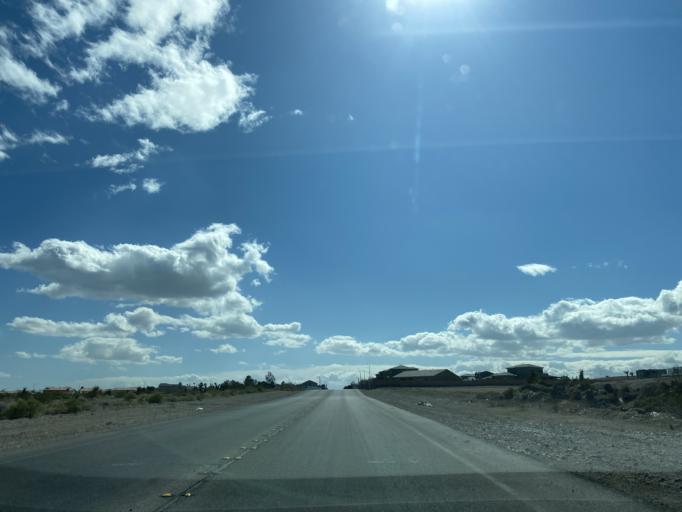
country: US
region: Nevada
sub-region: Clark County
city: Summerlin South
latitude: 36.2371
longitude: -115.3064
